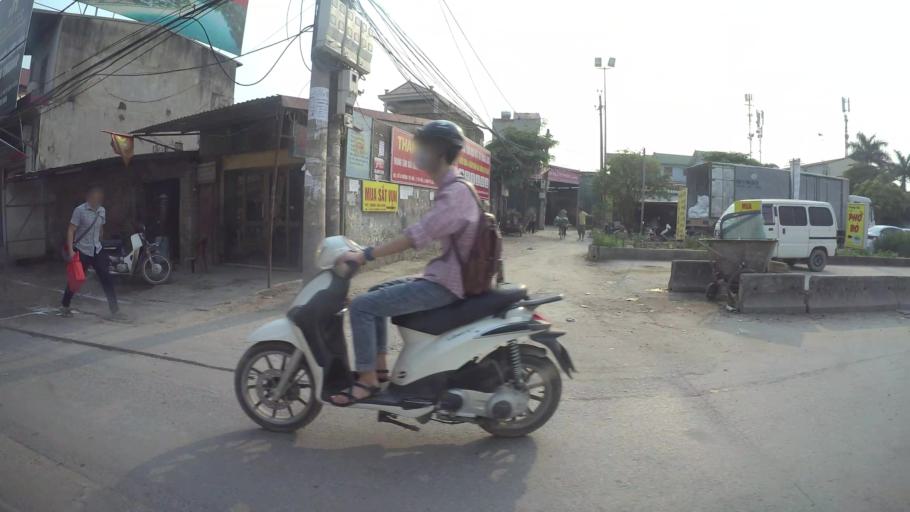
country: VN
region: Ha Noi
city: Cau Dien
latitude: 21.0055
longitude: 105.7491
